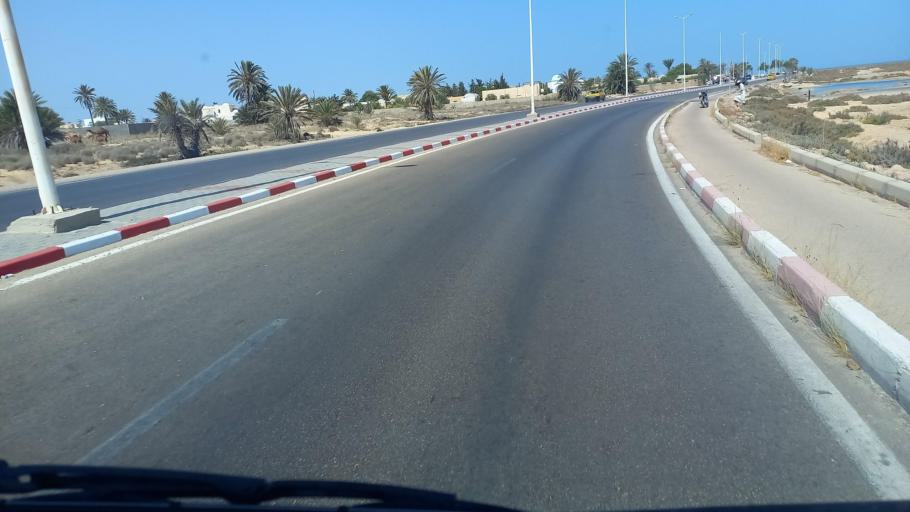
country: TN
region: Madanin
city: Houmt Souk
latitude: 33.8698
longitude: 10.9383
